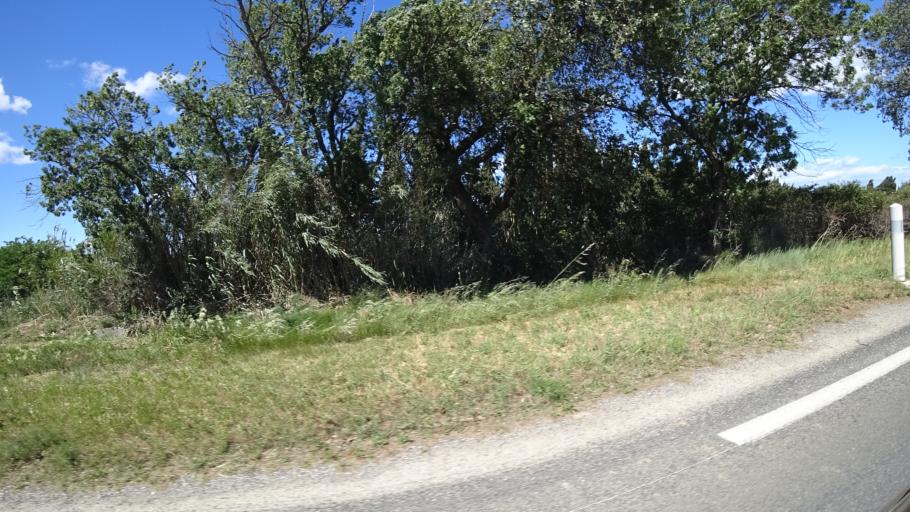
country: FR
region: Languedoc-Roussillon
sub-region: Departement des Pyrenees-Orientales
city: Saint-Nazaire
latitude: 42.6663
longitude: 2.9712
